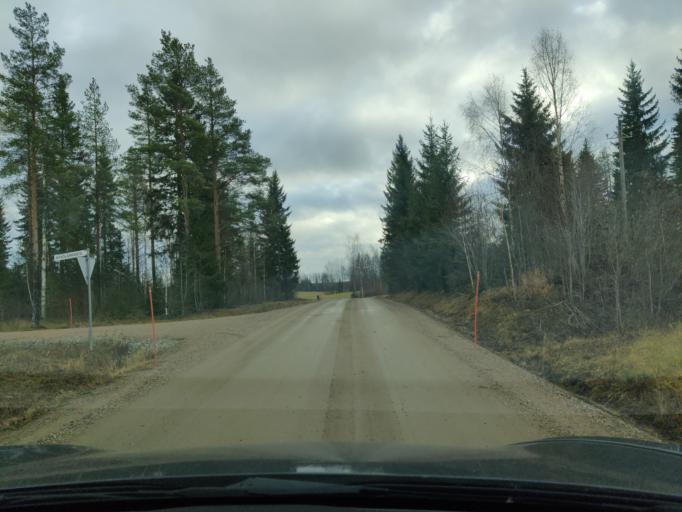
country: FI
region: Northern Savo
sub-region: Ylae-Savo
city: Kiuruvesi
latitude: 63.6381
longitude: 26.6462
